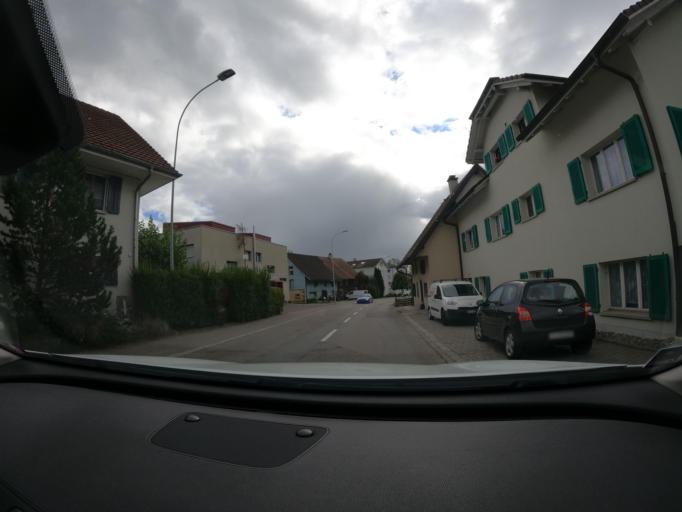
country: CH
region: Lucerne
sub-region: Sursee District
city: Bueron
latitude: 47.2118
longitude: 8.0918
